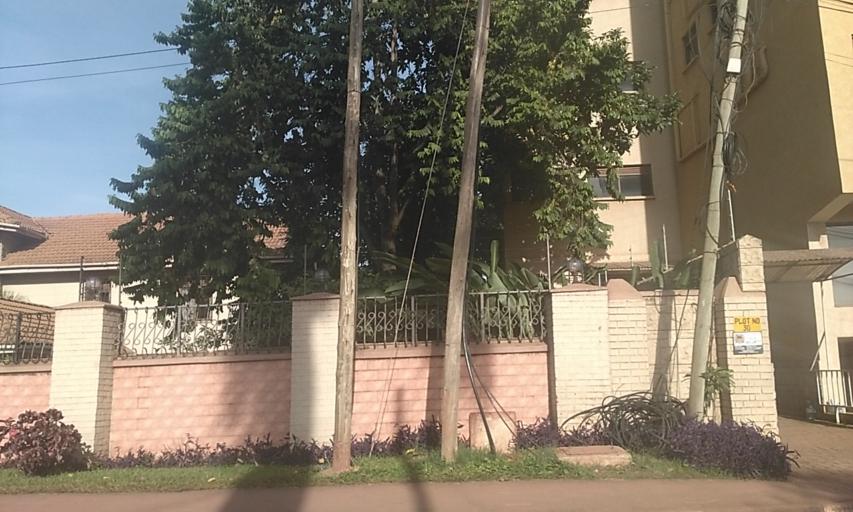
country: UG
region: Central Region
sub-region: Kampala District
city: Kampala
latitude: 0.3314
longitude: 32.6024
